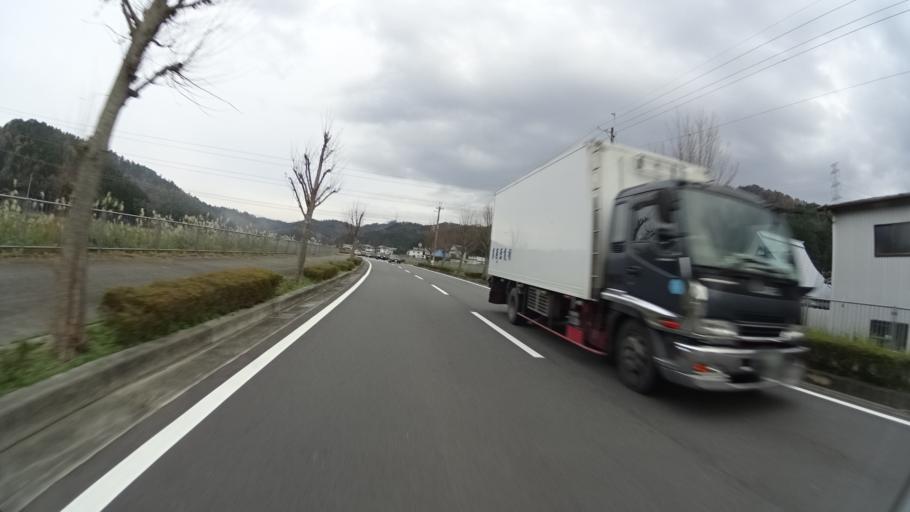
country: JP
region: Hyogo
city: Sasayama
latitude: 35.0730
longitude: 135.3632
